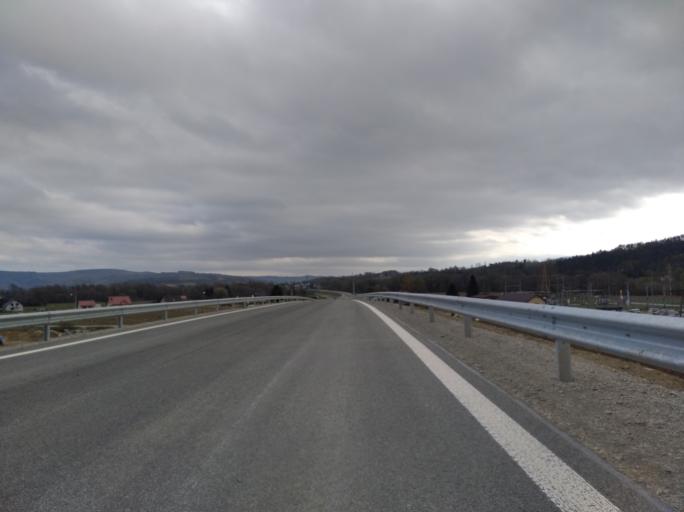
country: PL
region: Subcarpathian Voivodeship
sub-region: Powiat strzyzowski
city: Strzyzow
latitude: 49.8687
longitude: 21.7694
